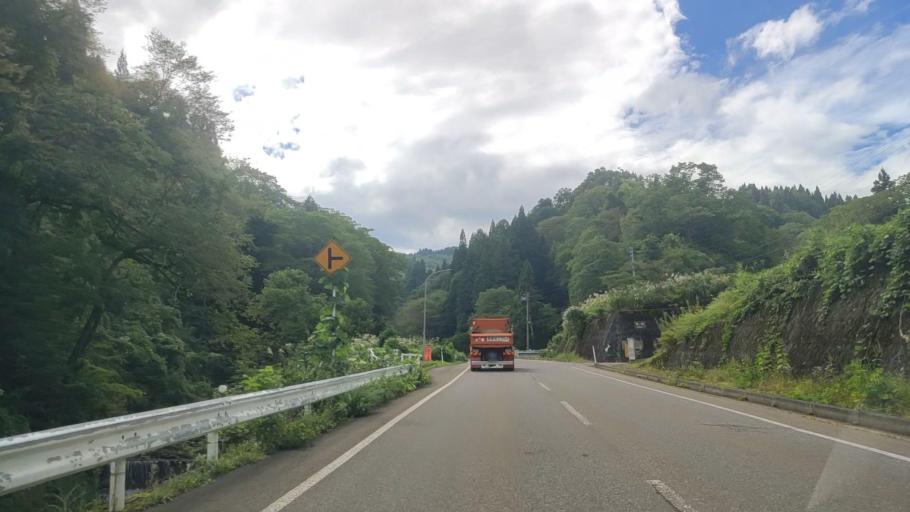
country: JP
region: Nagano
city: Iiyama
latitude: 36.9079
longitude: 138.3149
